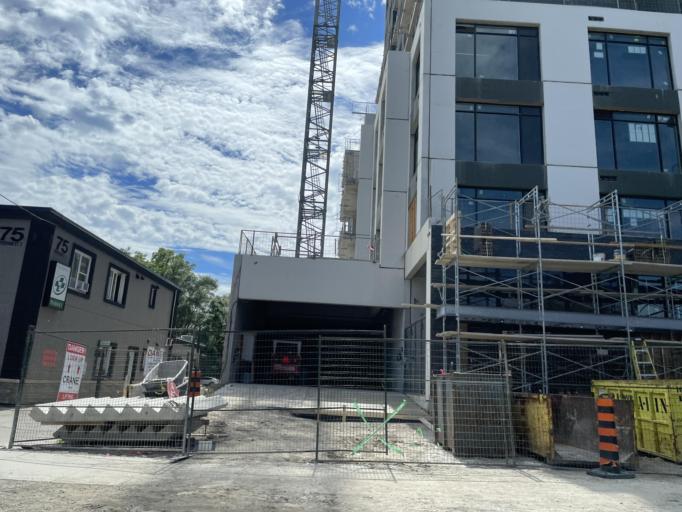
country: CA
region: Ontario
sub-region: Wellington County
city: Guelph
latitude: 43.5418
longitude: -80.2418
